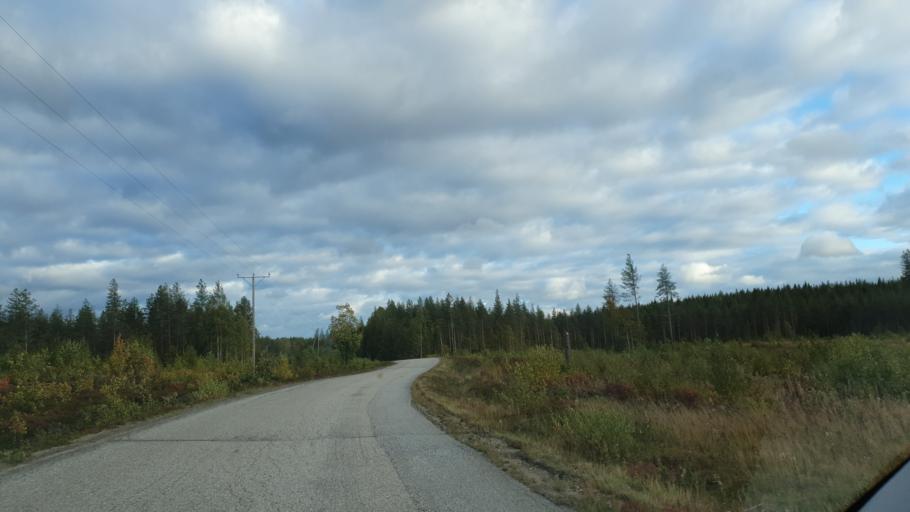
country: FI
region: North Karelia
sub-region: Pielisen Karjala
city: Lieksa
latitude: 63.9166
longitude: 30.1723
